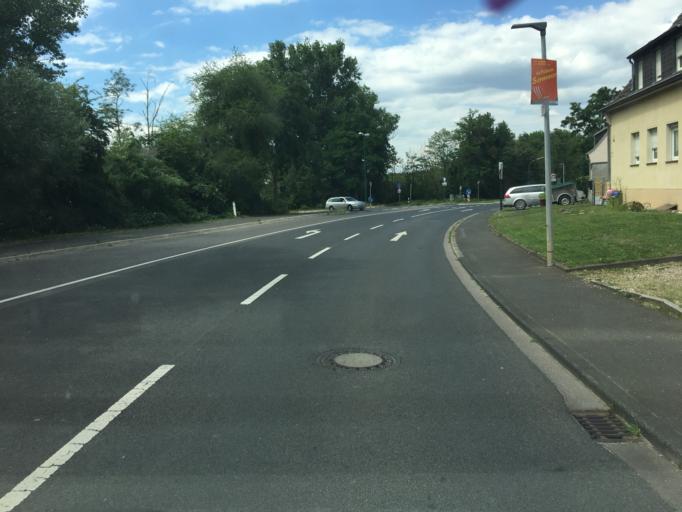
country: DE
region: North Rhine-Westphalia
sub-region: Regierungsbezirk Koln
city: Frechen
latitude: 50.8660
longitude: 6.8154
